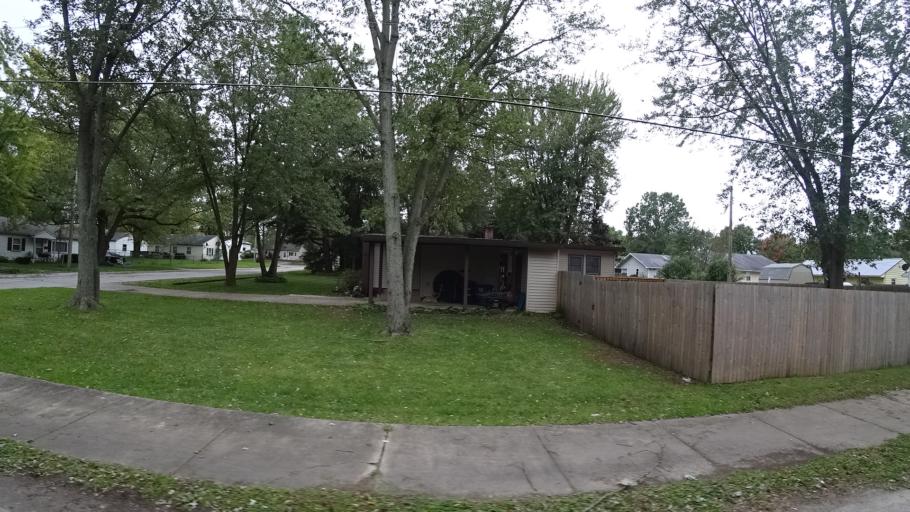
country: US
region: Indiana
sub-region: LaPorte County
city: Michigan City
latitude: 41.6973
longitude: -86.9017
